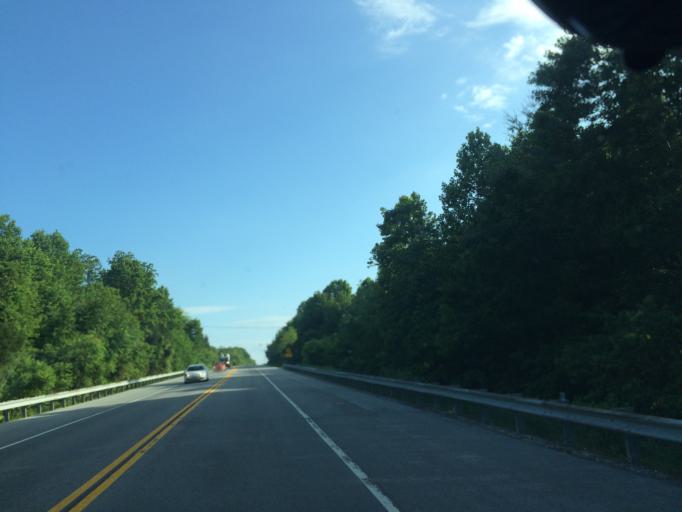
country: US
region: Maryland
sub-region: Carroll County
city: Westminster
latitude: 39.4879
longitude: -76.9969
